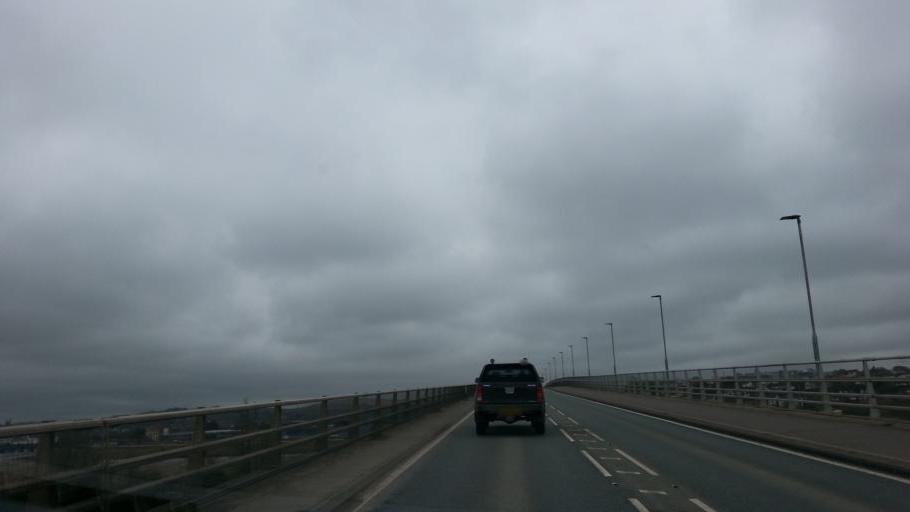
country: GB
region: England
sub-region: Devon
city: Barnstaple
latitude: 51.0814
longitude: -4.0722
